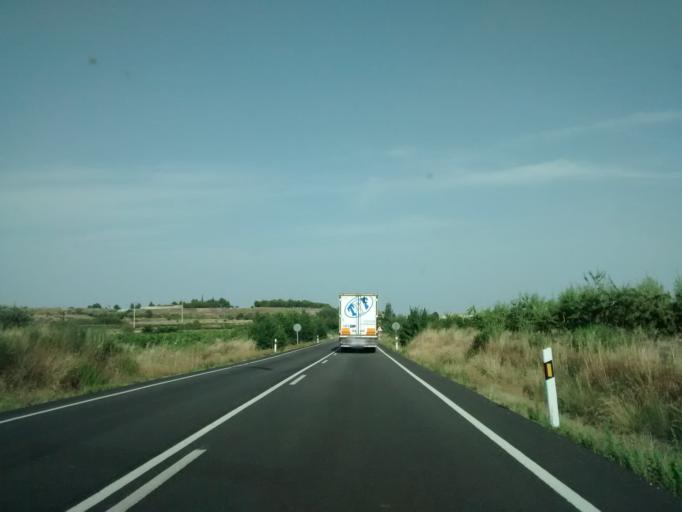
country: ES
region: Aragon
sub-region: Provincia de Zaragoza
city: Malejan
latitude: 41.8302
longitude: -1.5624
